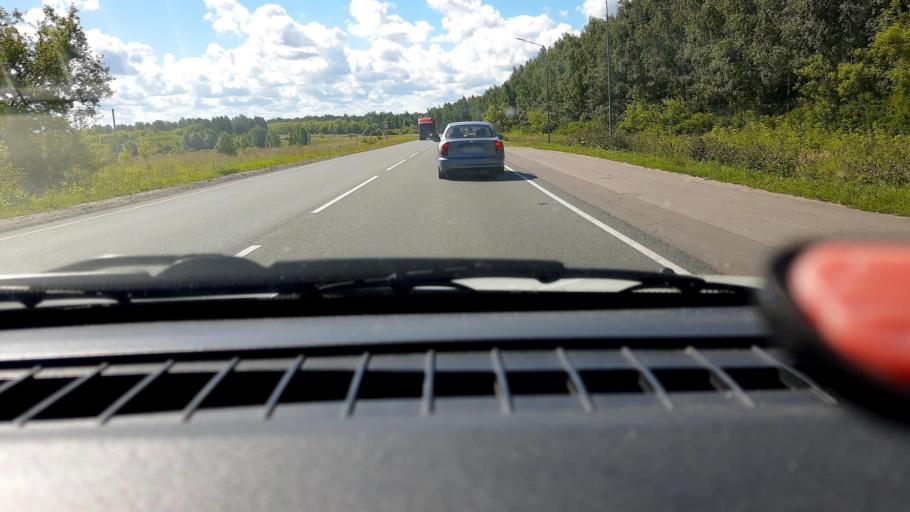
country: RU
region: Nizjnij Novgorod
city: Arzamas
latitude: 55.3217
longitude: 43.8883
